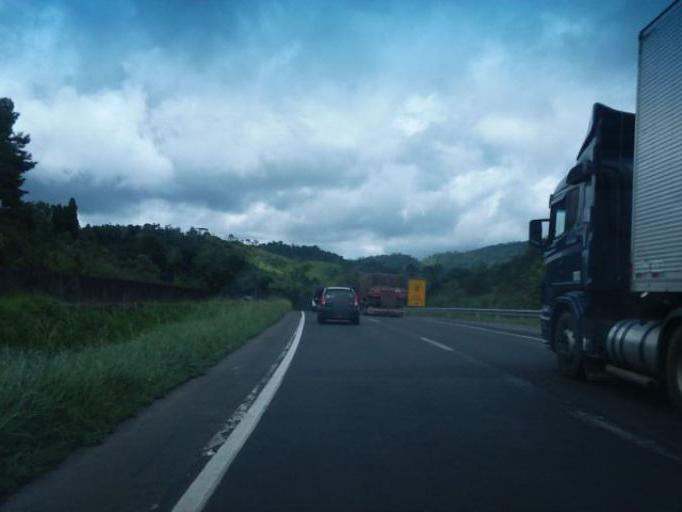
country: BR
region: Parana
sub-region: Antonina
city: Antonina
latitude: -25.0236
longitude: -48.5172
